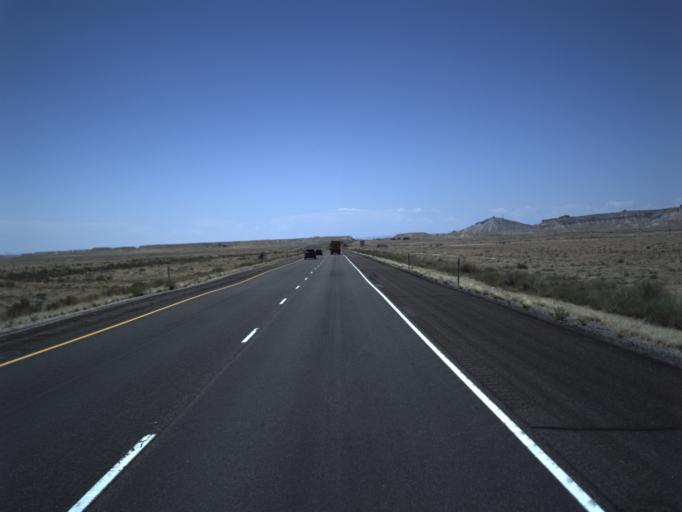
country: US
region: Utah
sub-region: Grand County
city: Moab
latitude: 38.9513
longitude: -109.7728
